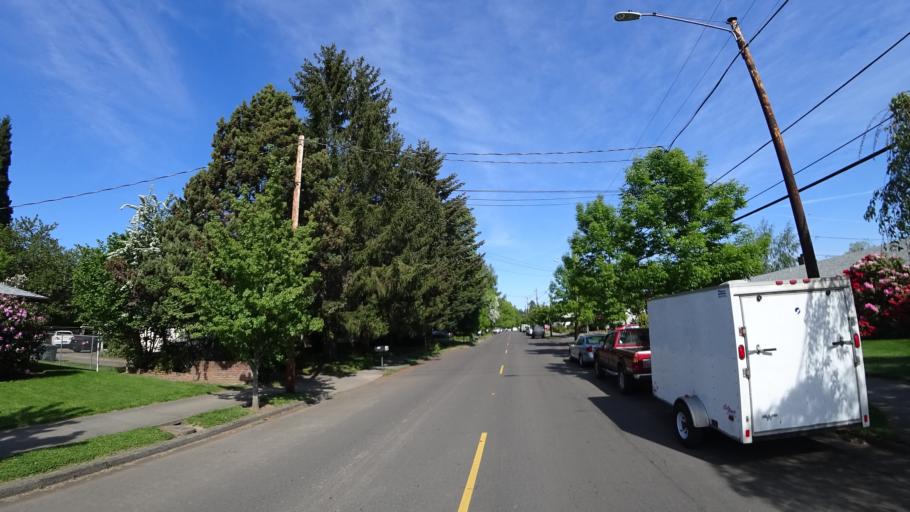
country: US
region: Oregon
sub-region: Washington County
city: Hillsboro
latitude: 45.5174
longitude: -122.9689
